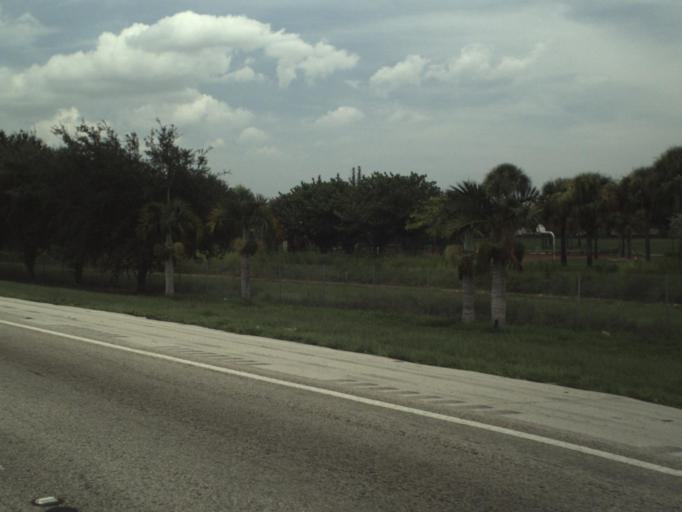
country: US
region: Florida
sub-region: Broward County
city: Kendall Green
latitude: 26.2494
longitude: -80.1364
